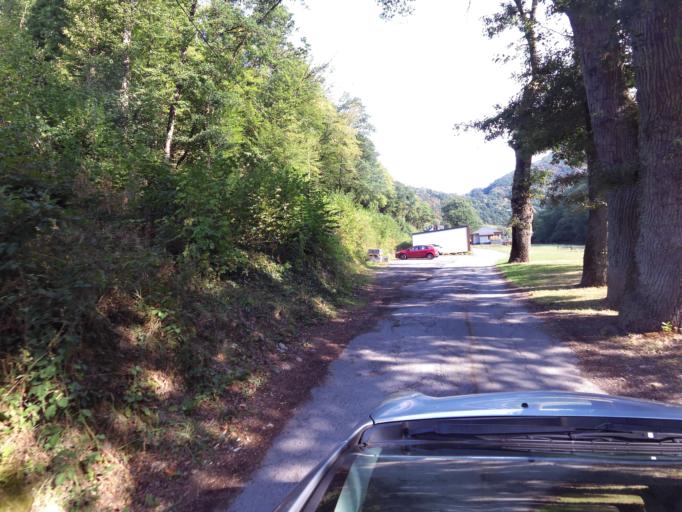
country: LU
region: Diekirch
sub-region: Canton de Diekirch
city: Bourscheid
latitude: 49.9094
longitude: 6.0817
